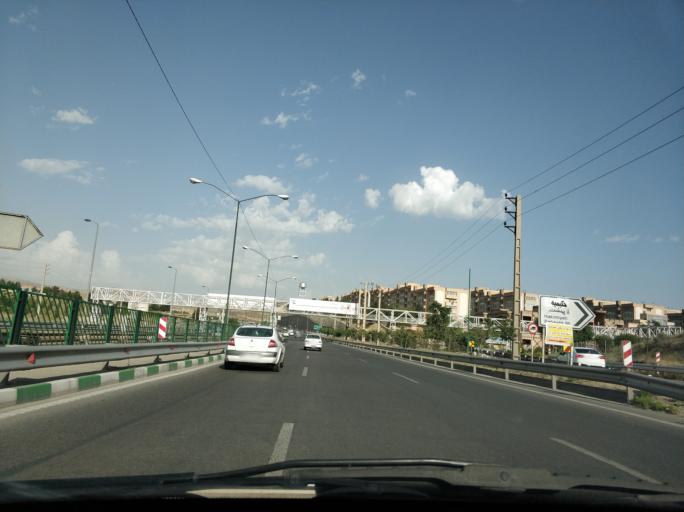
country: IR
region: Tehran
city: Tajrish
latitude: 35.7461
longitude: 51.5987
